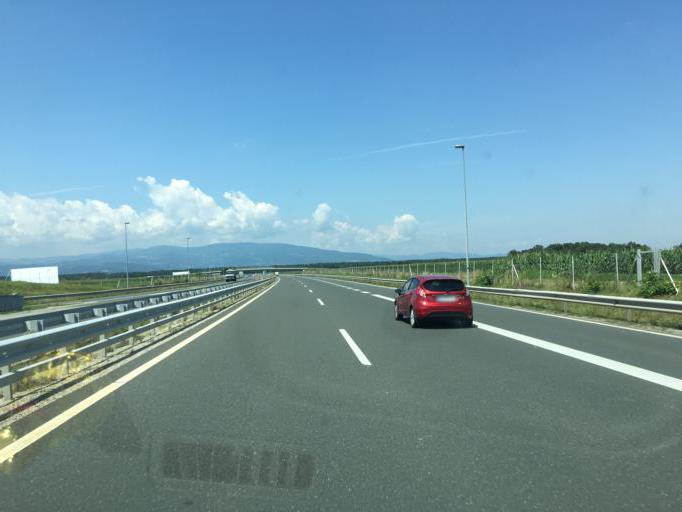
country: SI
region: Starse
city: Starse
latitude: 46.4537
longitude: 15.7562
